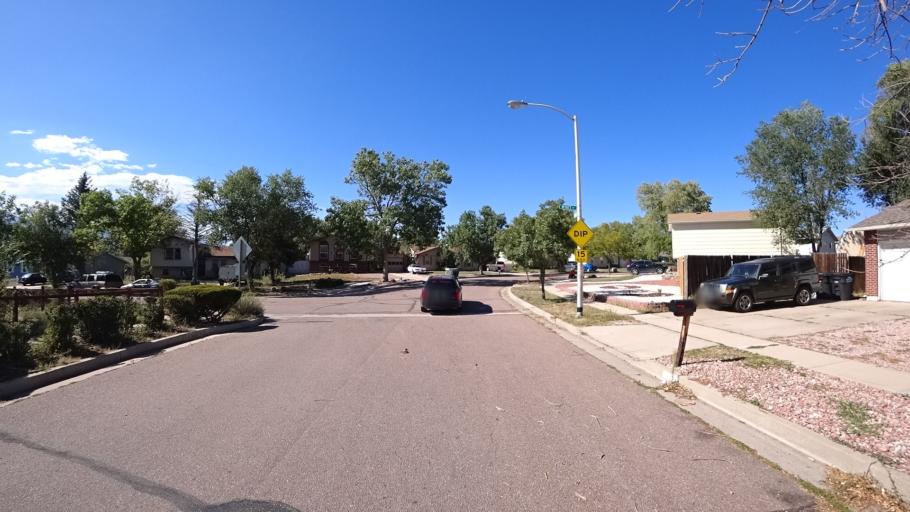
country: US
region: Colorado
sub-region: El Paso County
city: Stratmoor
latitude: 38.7910
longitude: -104.7478
